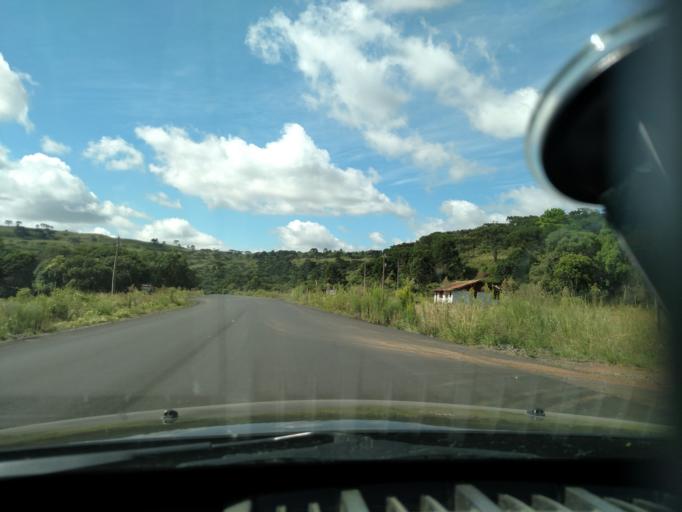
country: BR
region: Santa Catarina
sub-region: Sao Joaquim
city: Sao Joaquim
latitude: -28.1256
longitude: -50.0509
